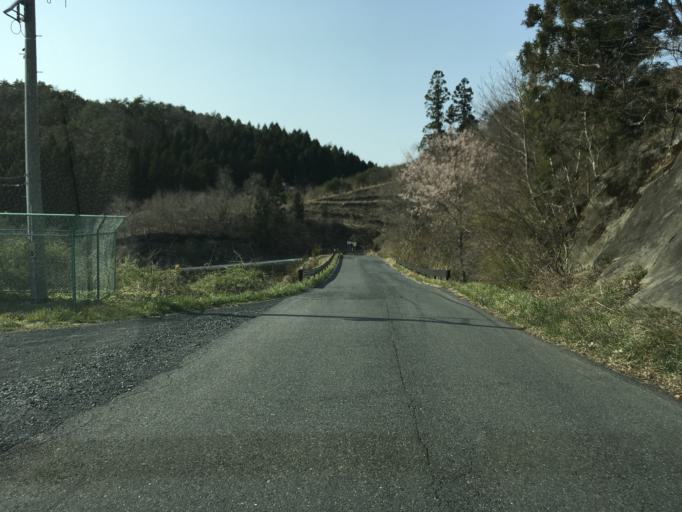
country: JP
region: Iwate
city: Ichinoseki
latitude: 38.8209
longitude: 141.3155
